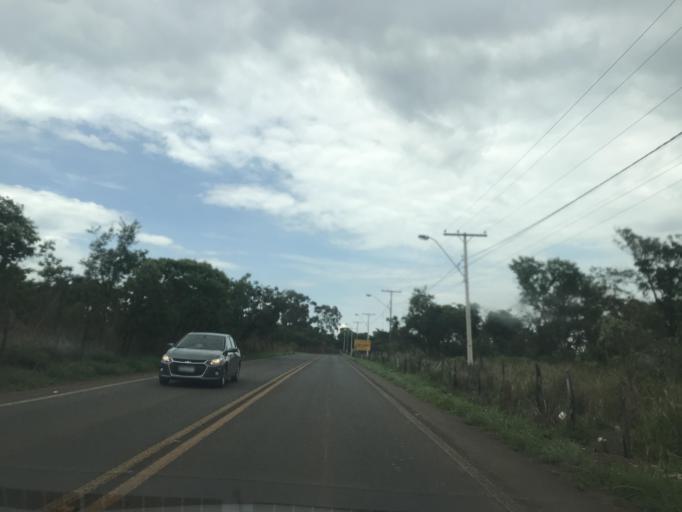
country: BR
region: Goias
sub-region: Luziania
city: Luziania
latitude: -16.2573
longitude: -47.9698
